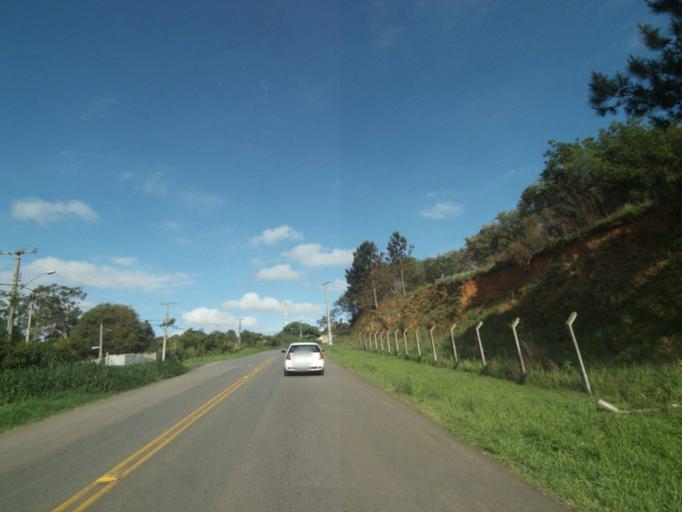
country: BR
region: Parana
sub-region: Curitiba
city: Curitiba
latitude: -25.3917
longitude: -49.3008
